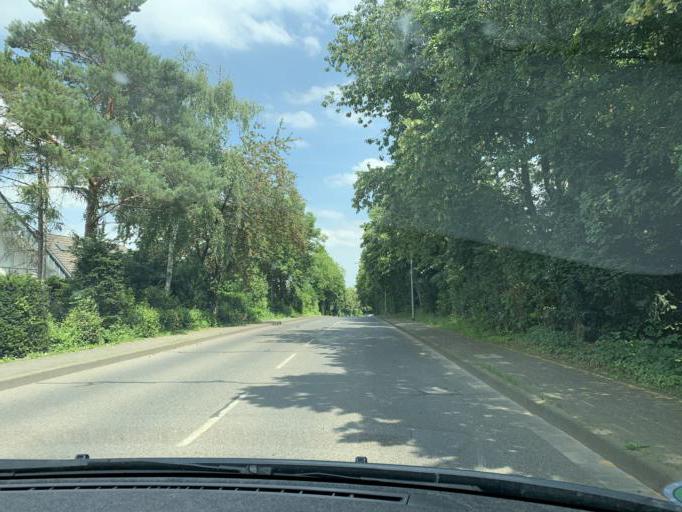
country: DE
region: North Rhine-Westphalia
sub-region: Regierungsbezirk Koln
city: Bedburg
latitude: 50.9903
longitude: 6.5657
